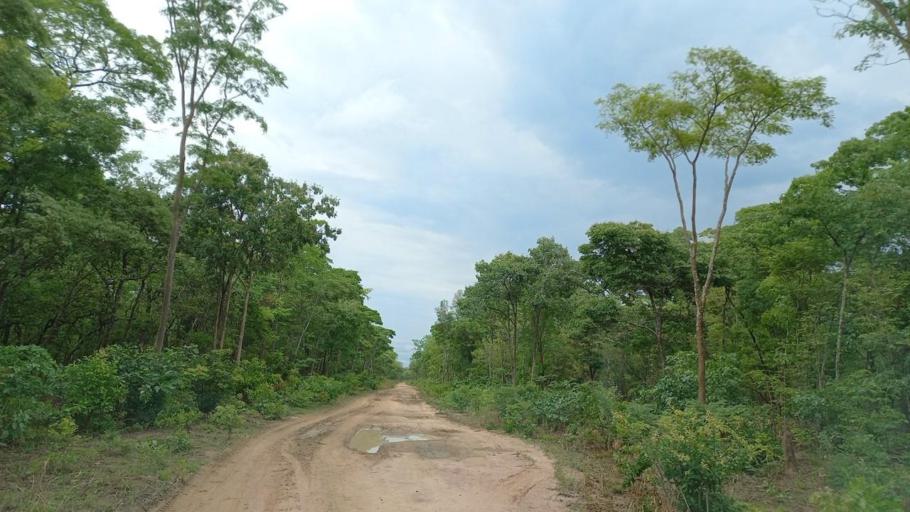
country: ZM
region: North-Western
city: Kalengwa
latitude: -13.5565
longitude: 24.9740
